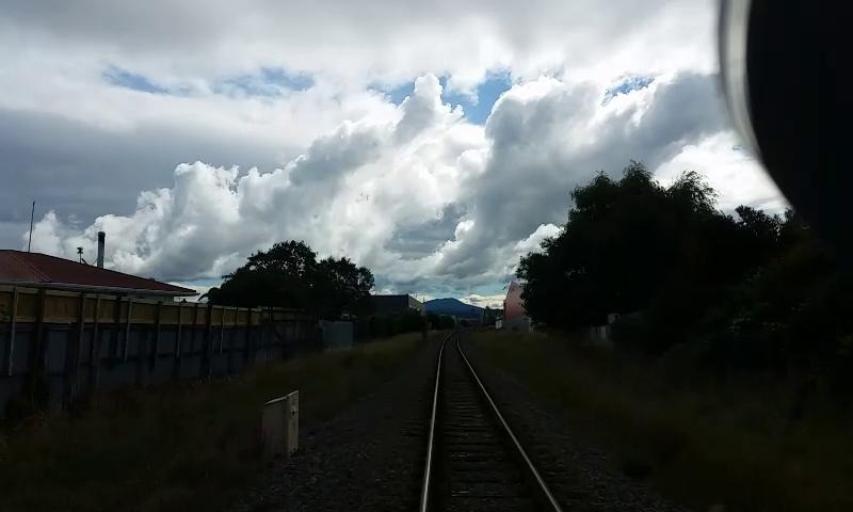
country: NZ
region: Canterbury
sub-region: Waimakariri District
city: Woodend
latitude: -43.3056
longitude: 172.5989
